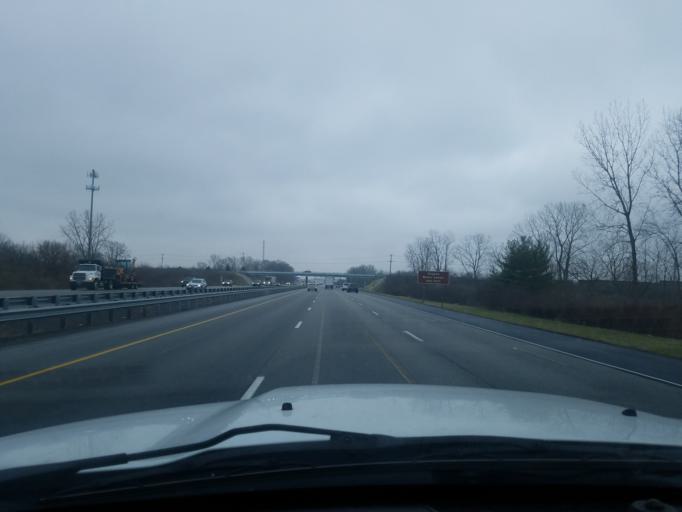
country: US
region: Indiana
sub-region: Hamilton County
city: Fishers
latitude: 39.9837
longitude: -85.9430
